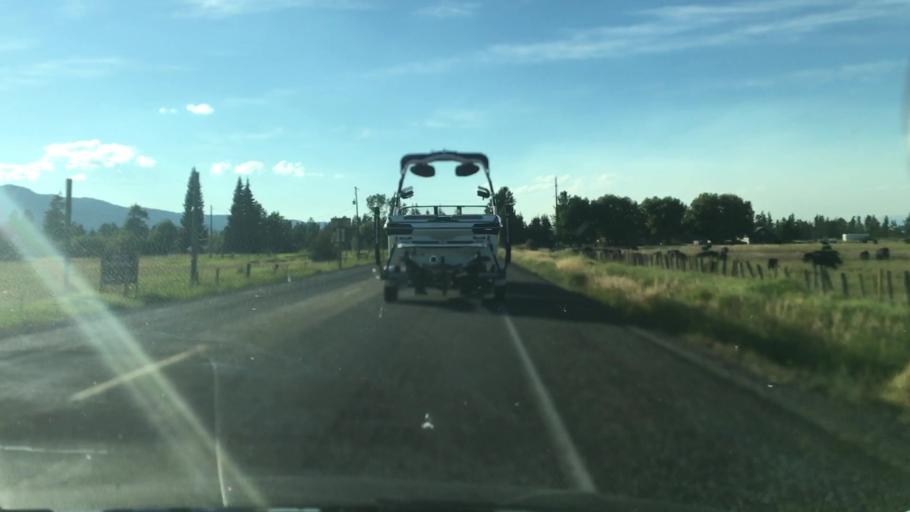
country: US
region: Idaho
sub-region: Valley County
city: McCall
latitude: 44.7227
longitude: -116.0696
